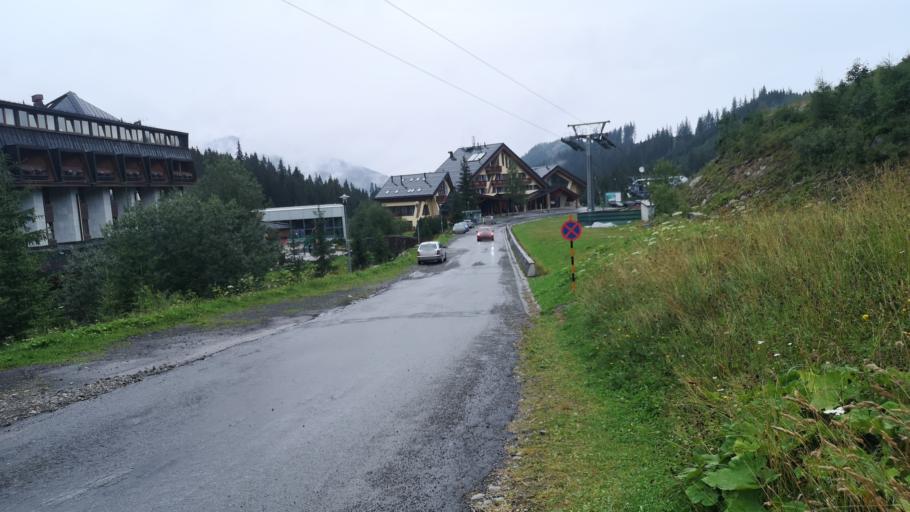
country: SK
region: Zilinsky
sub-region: Okres Liptovsky Mikulas
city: Liptovsky Mikulas
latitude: 48.9696
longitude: 19.5811
